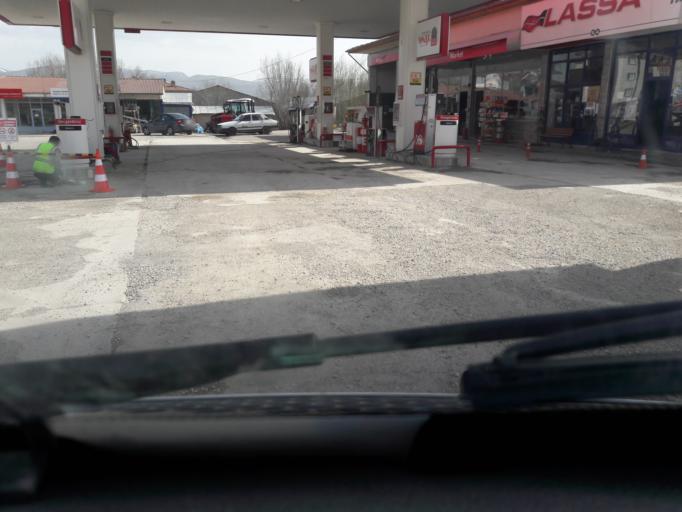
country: TR
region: Gumushane
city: Kelkit
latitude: 40.1421
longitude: 39.4330
